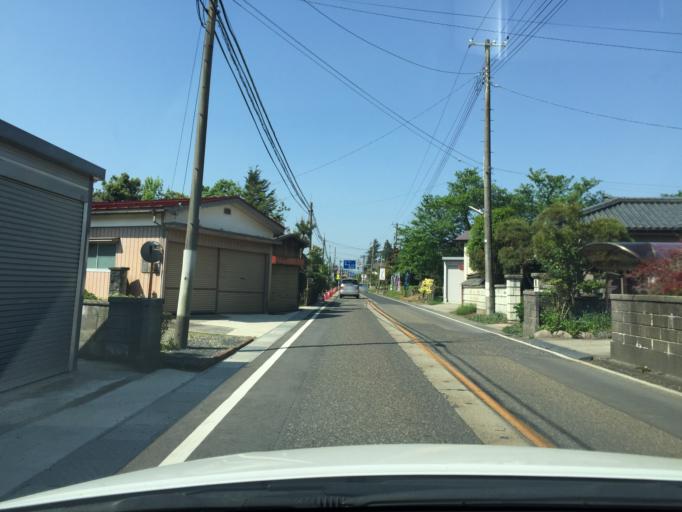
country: JP
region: Niigata
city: Muramatsu
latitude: 37.7015
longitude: 139.1921
